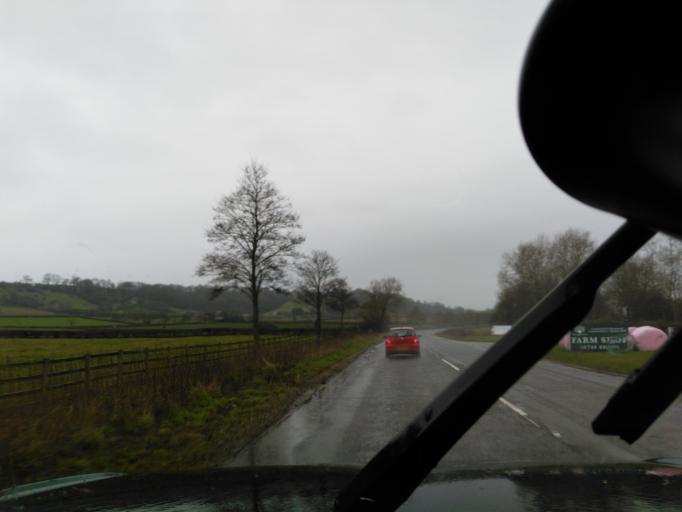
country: GB
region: England
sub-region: Somerset
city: Wells
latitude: 51.1547
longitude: -2.6158
